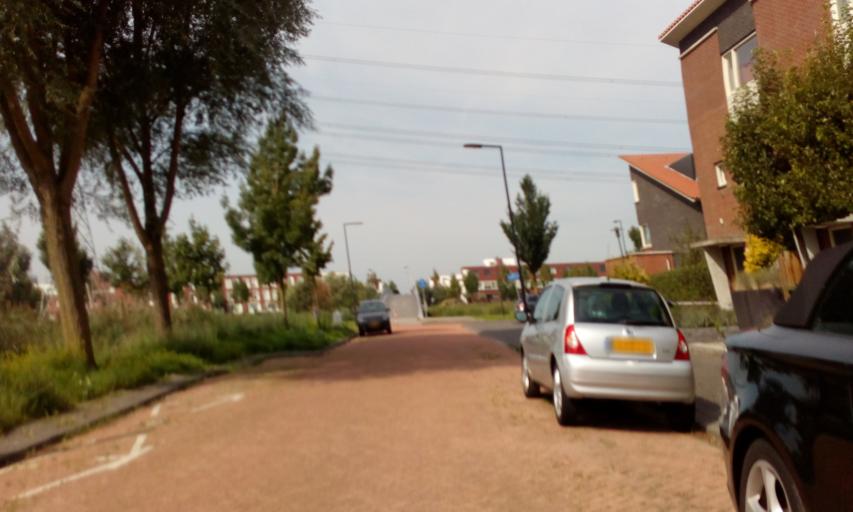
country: NL
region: South Holland
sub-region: Gemeente Capelle aan den IJssel
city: Capelle aan den IJssel
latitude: 51.9850
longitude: 4.5885
